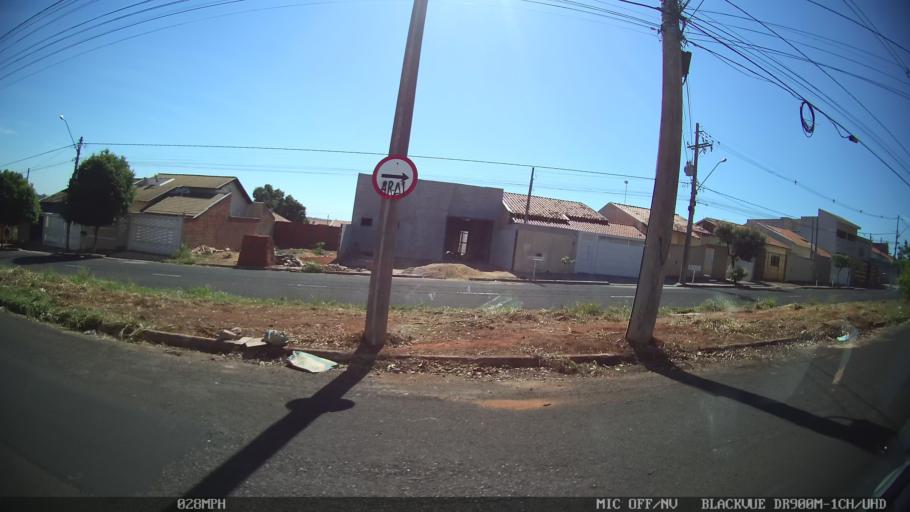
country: BR
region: Sao Paulo
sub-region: Sao Jose Do Rio Preto
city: Sao Jose do Rio Preto
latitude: -20.7665
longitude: -49.4138
